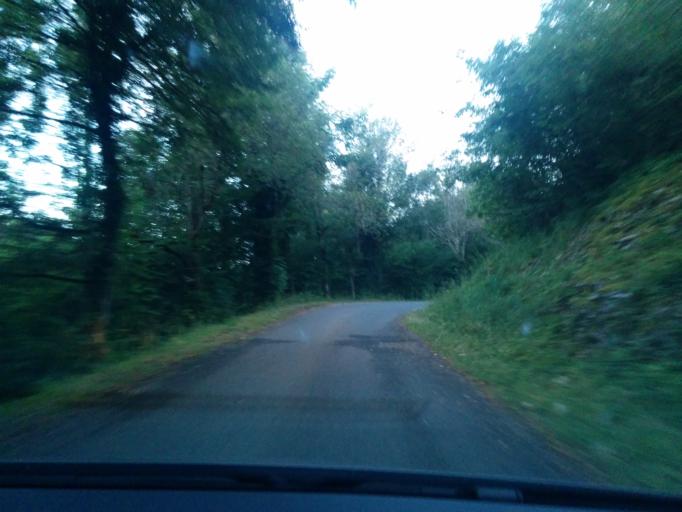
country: FR
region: Franche-Comte
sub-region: Departement du Jura
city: Valfin-les-Saint-Claude
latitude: 46.4430
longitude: 5.8247
